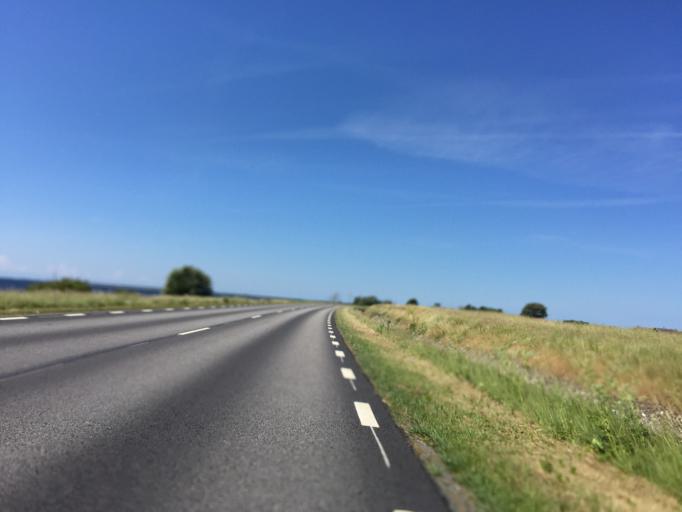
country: SE
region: Skane
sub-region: Trelleborgs Kommun
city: Skare
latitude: 55.3829
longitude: 13.0265
